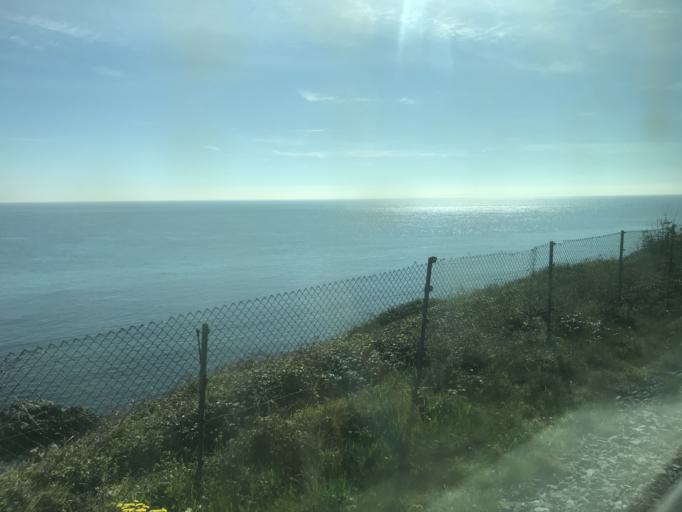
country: IE
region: Leinster
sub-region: Wicklow
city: Bray
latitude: 53.1939
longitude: -6.0841
